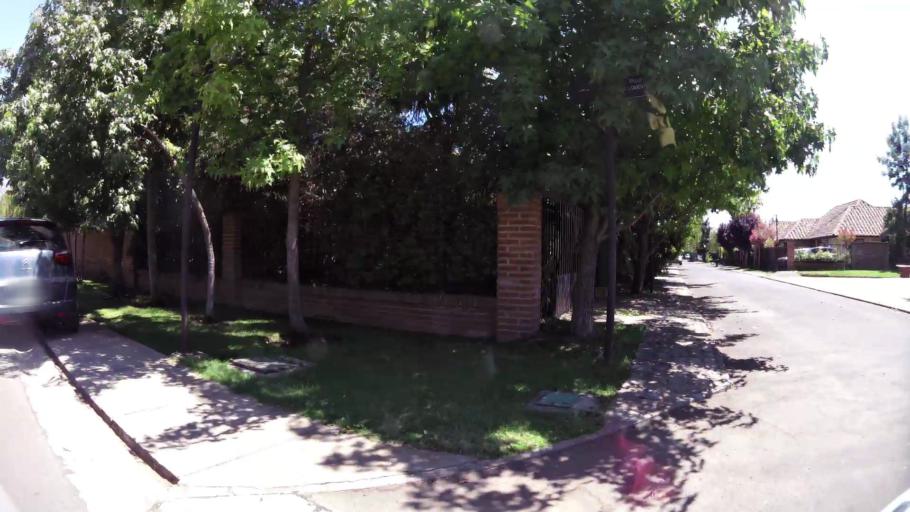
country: CL
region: Maule
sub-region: Provincia de Talca
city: Talca
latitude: -35.4336
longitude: -71.6250
